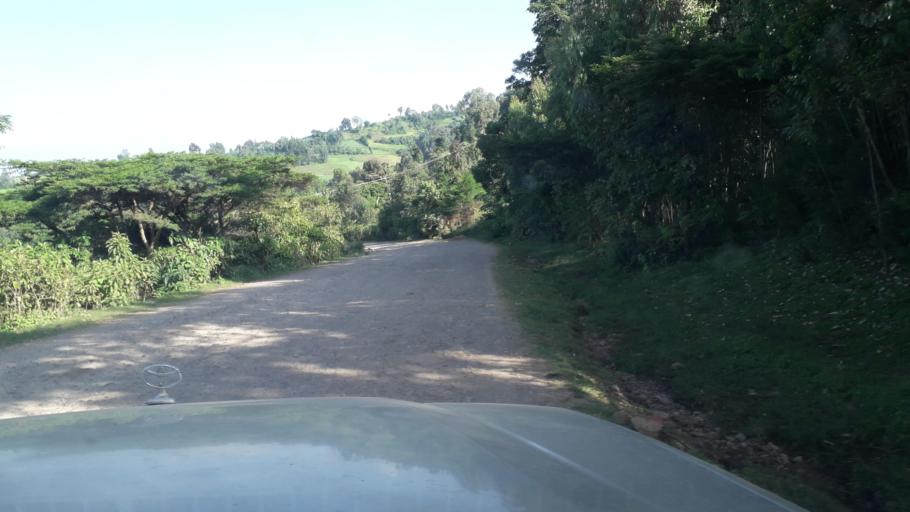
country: ET
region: Oromiya
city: Jima
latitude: 7.4647
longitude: 36.8730
